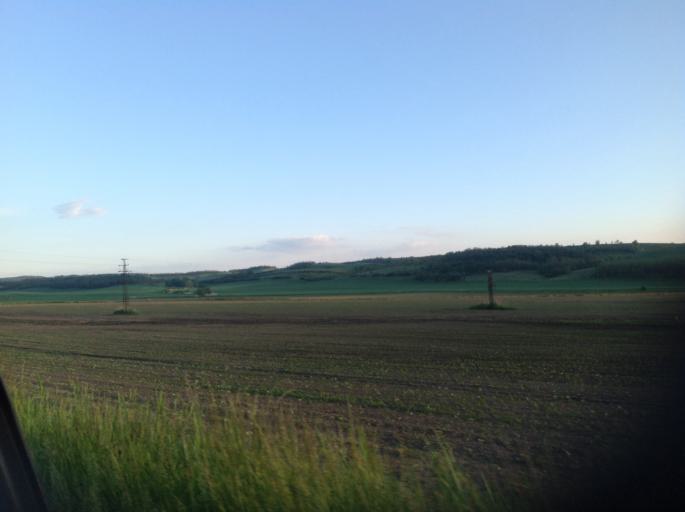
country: HU
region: Komarom-Esztergom
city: Sarisap
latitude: 47.6617
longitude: 18.6990
